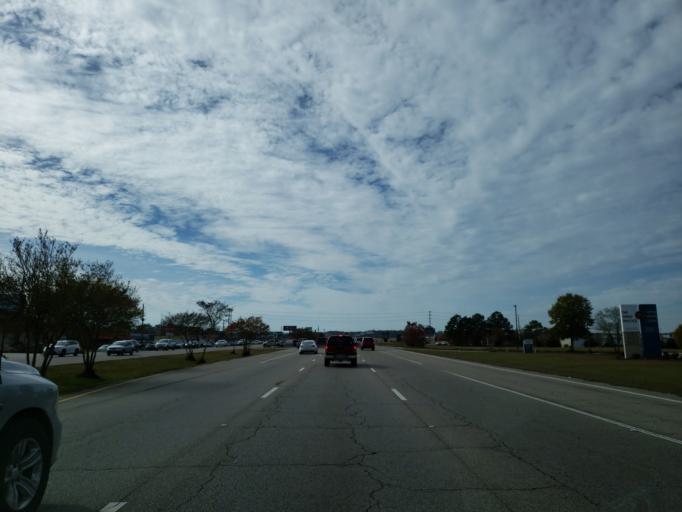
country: US
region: Mississippi
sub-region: Lamar County
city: West Hattiesburg
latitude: 31.3228
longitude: -89.3696
